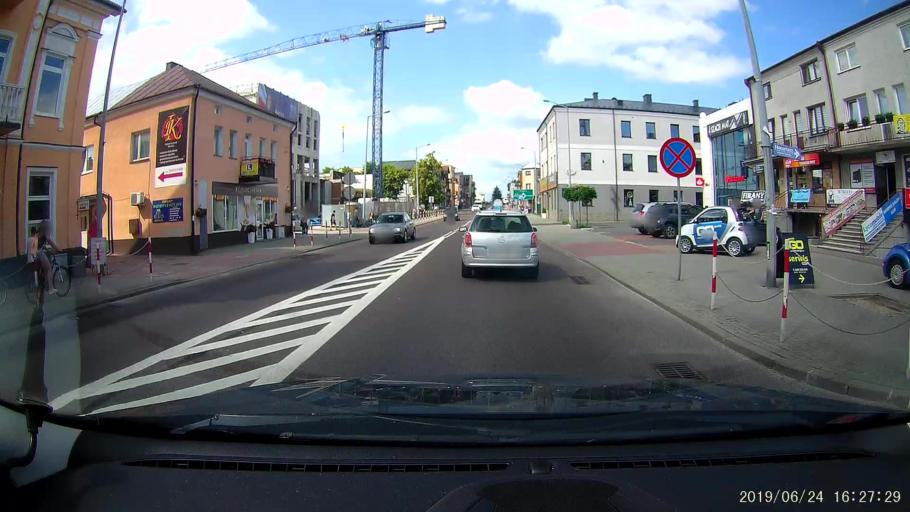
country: PL
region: Lublin Voivodeship
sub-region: Powiat tomaszowski
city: Tomaszow Lubelski
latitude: 50.4507
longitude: 23.4179
